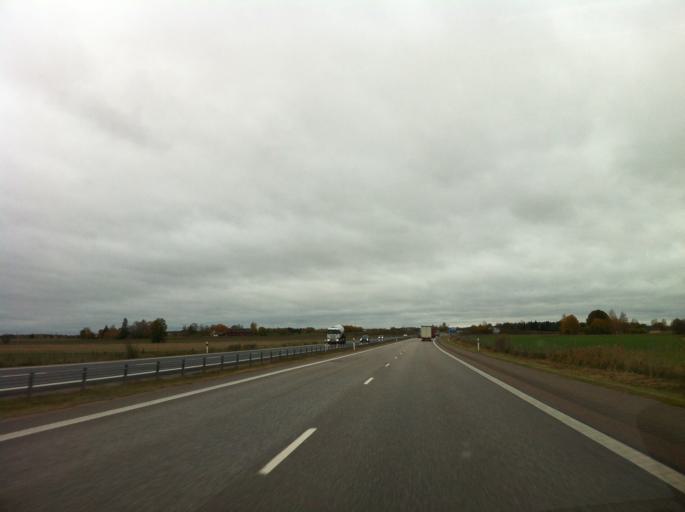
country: SE
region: OEstergoetland
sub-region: Mjolby Kommun
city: Mantorp
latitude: 58.3783
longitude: 15.3391
